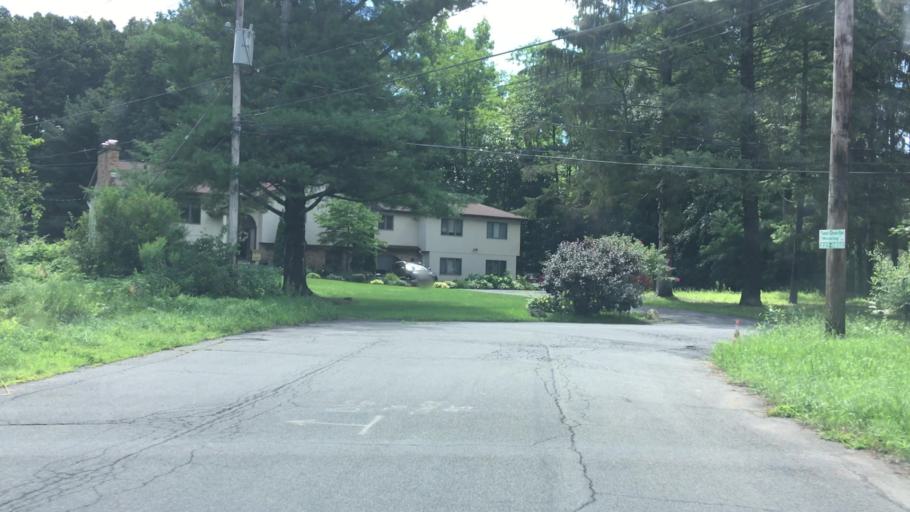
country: US
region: New York
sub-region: Albany County
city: Colonie
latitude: 42.7408
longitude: -73.8551
